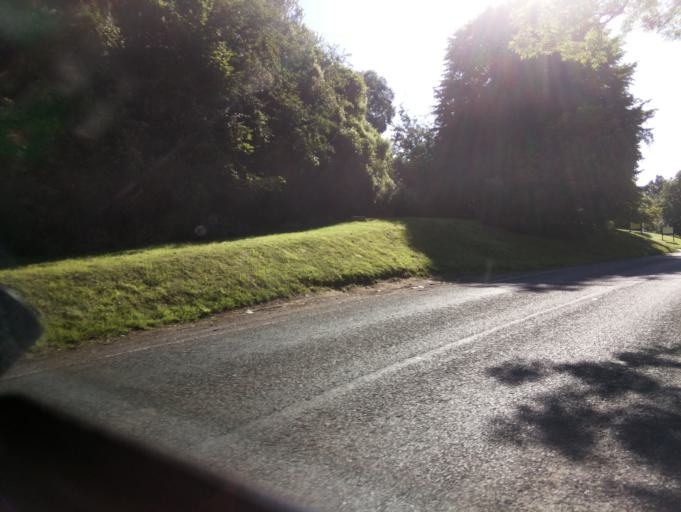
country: GB
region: England
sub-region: Herefordshire
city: Walford
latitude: 51.8652
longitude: -2.6047
